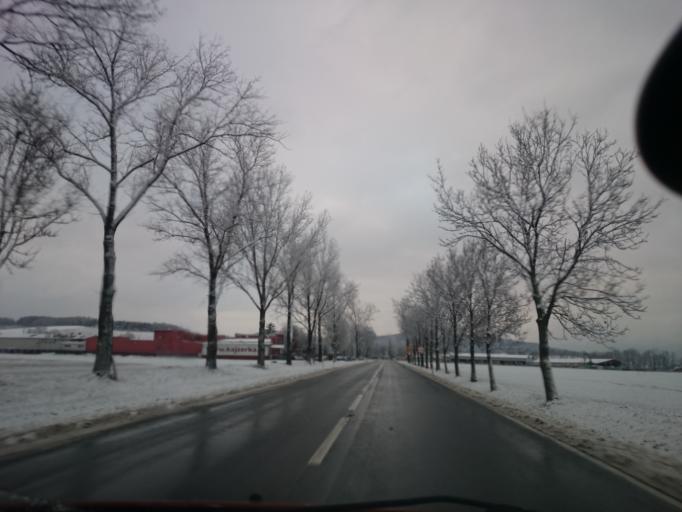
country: PL
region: Lower Silesian Voivodeship
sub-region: Powiat klodzki
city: Klodzko
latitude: 50.3948
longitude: 16.6596
